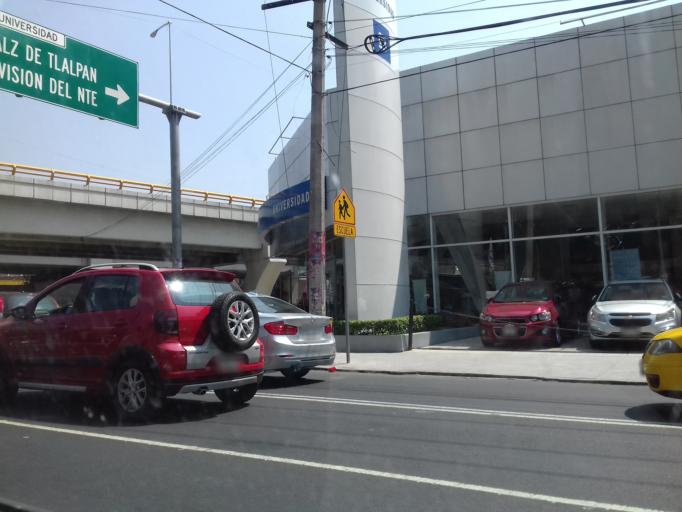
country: MX
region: Mexico City
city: Coyoacan
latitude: 19.3591
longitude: -99.1719
